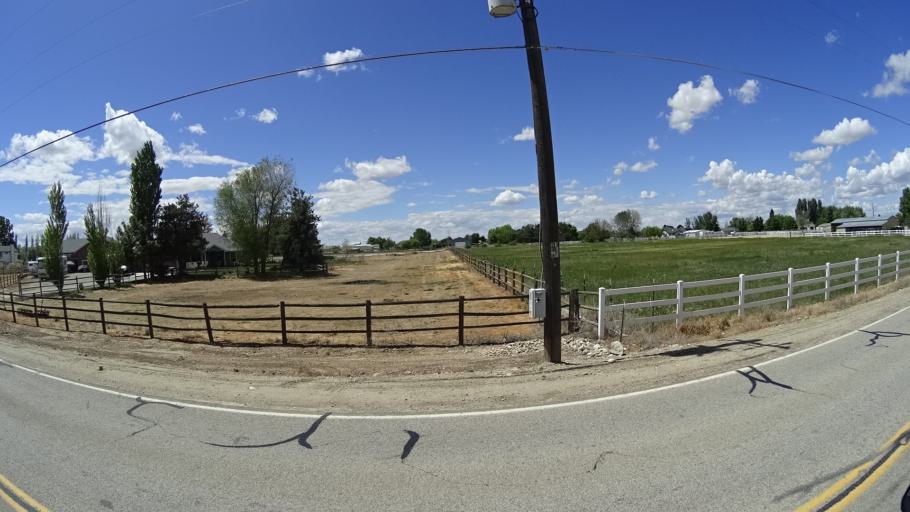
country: US
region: Idaho
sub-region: Ada County
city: Meridian
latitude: 43.5817
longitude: -116.4337
